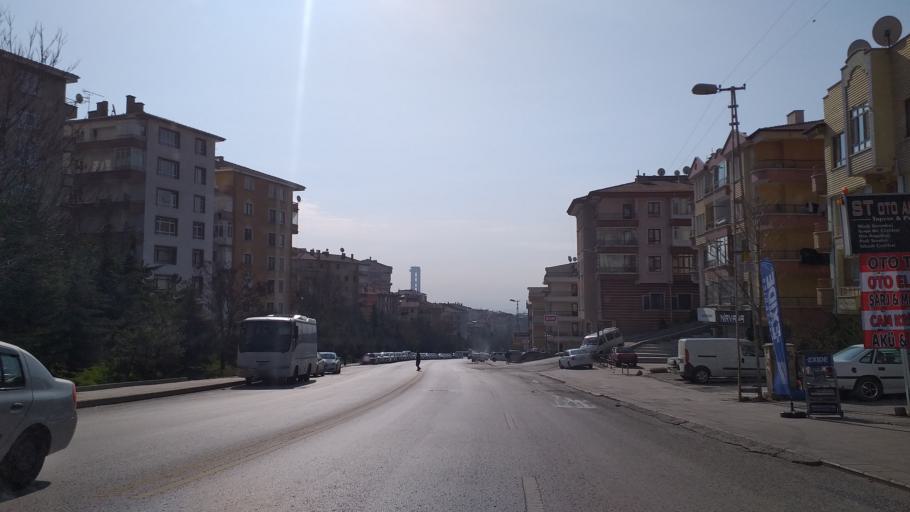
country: TR
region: Ankara
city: Ankara
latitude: 39.9956
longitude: 32.8546
